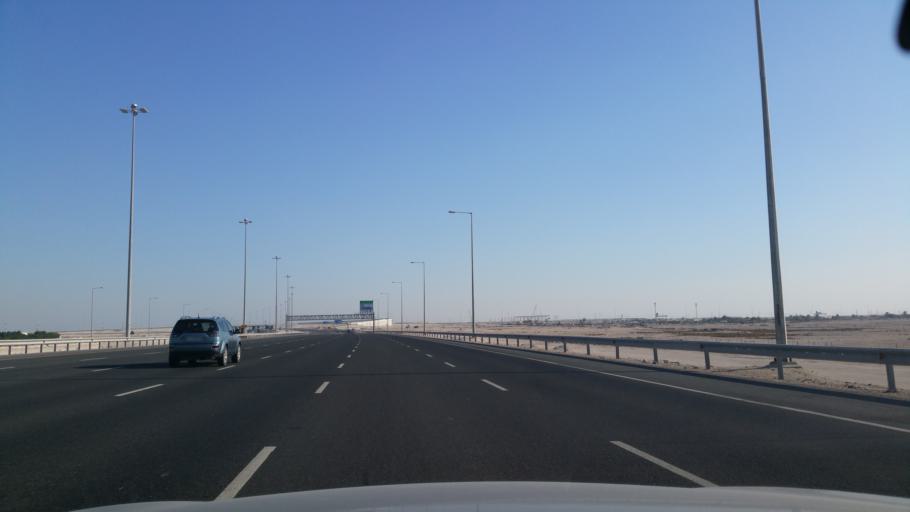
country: QA
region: Al Wakrah
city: Al Wukayr
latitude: 25.1335
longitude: 51.4791
